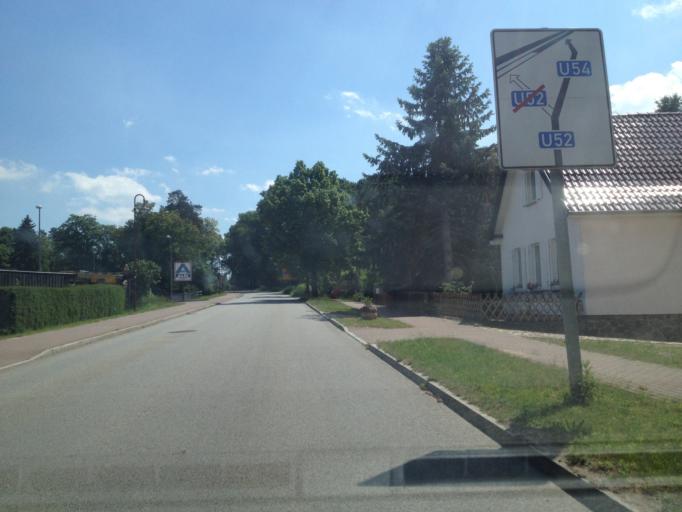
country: DE
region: Brandenburg
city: Joachimsthal
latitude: 52.9749
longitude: 13.7545
